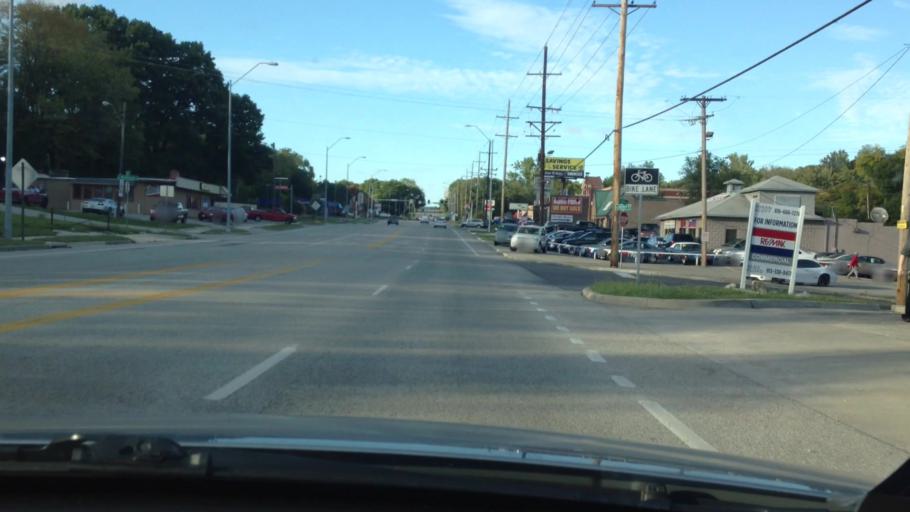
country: US
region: Missouri
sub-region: Platte County
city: Riverside
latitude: 39.1680
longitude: -94.5767
